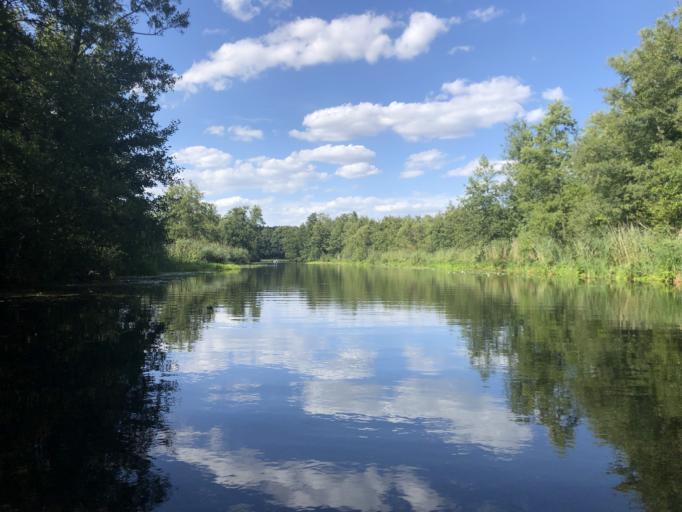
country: DE
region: Brandenburg
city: Mullrose
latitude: 52.2477
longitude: 14.4302
